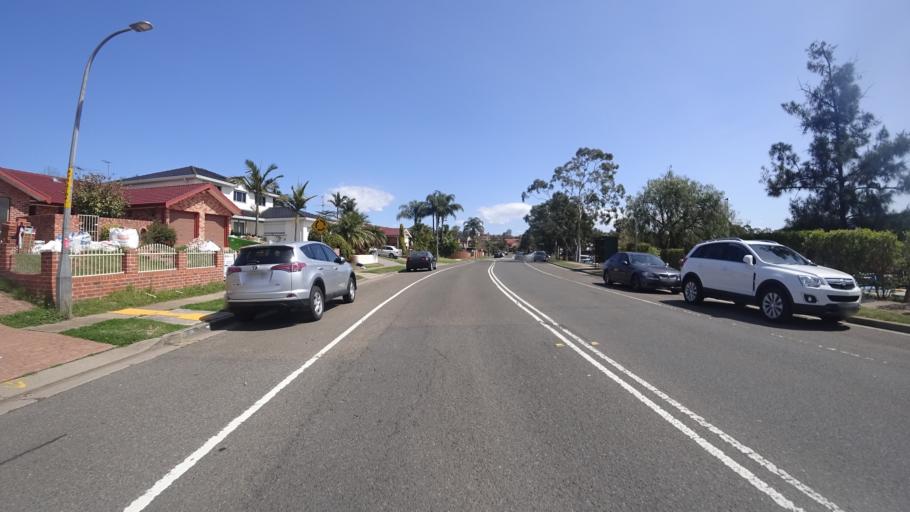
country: AU
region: New South Wales
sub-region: Campbelltown Municipality
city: Glenfield
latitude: -33.9492
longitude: 150.9001
